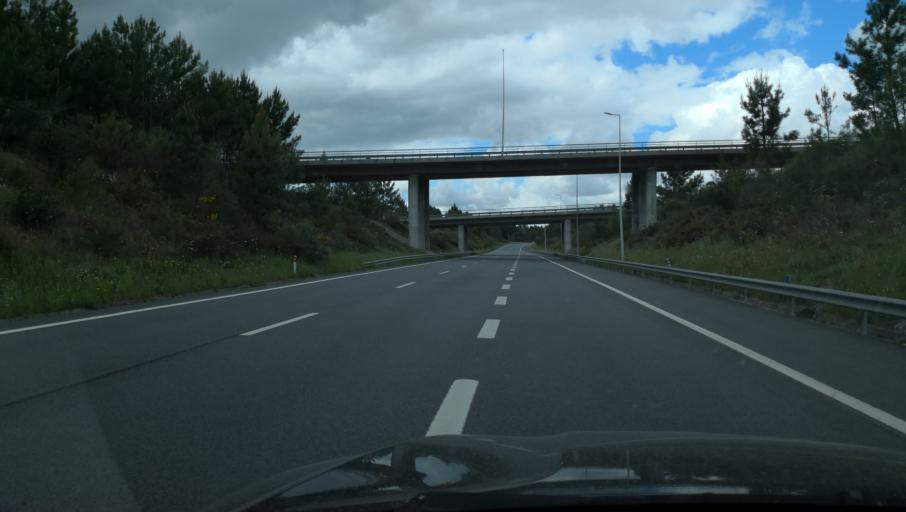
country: PT
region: Evora
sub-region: Vendas Novas
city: Vendas Novas
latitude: 38.6040
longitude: -8.6441
